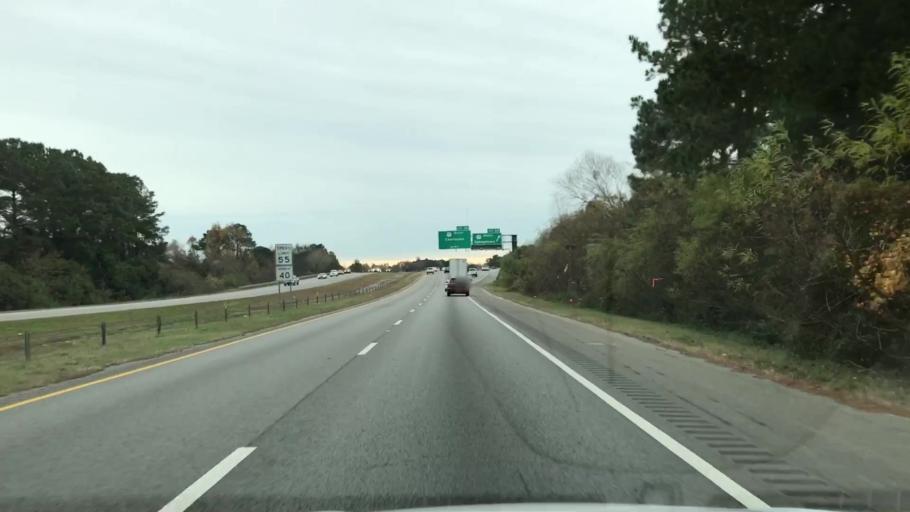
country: US
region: South Carolina
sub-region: Charleston County
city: Mount Pleasant
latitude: 32.8269
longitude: -79.8511
